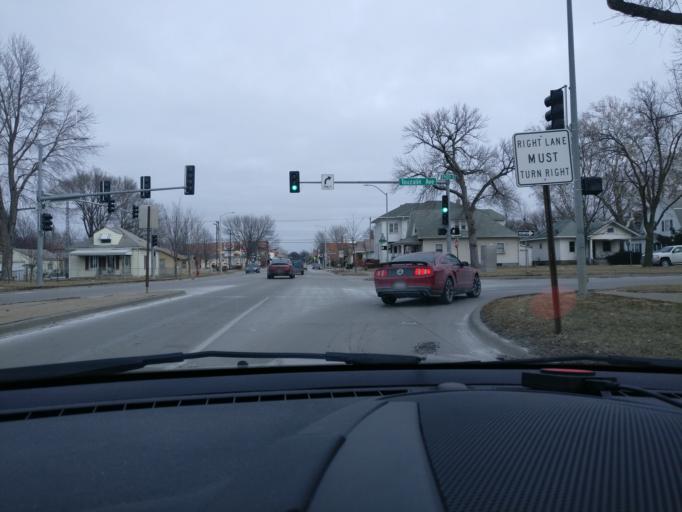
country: US
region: Nebraska
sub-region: Lancaster County
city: Lincoln
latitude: 40.8571
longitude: -96.6405
